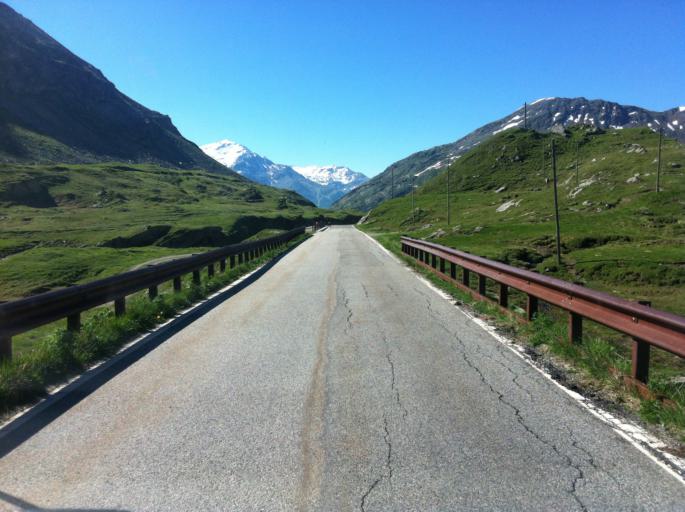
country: IT
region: Lombardy
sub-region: Provincia di Sondrio
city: Campodolcino
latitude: 46.5036
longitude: 9.3308
